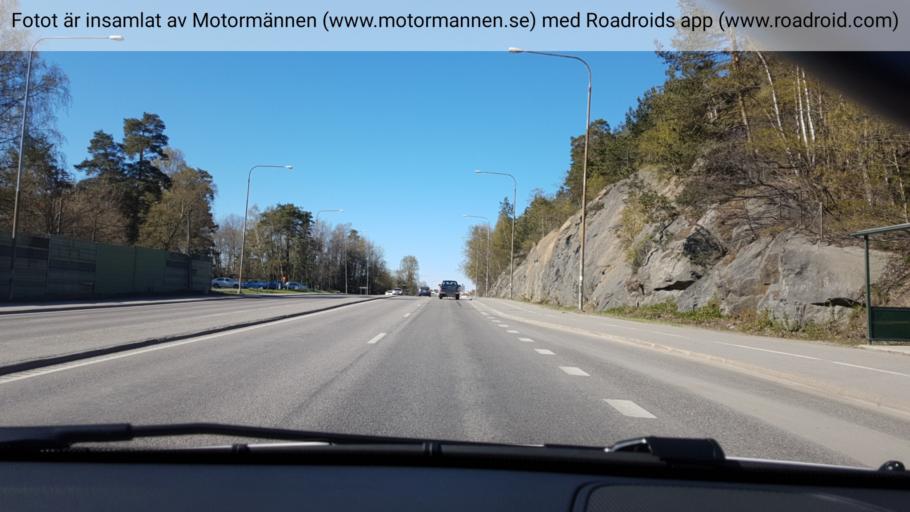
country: SE
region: Stockholm
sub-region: Huddinge Kommun
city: Huddinge
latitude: 59.2479
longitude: 18.0046
